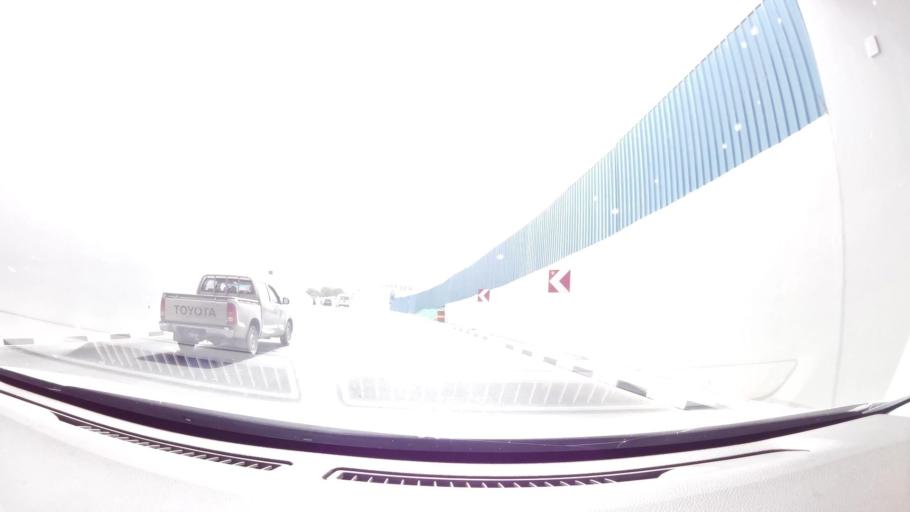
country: QA
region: Baladiyat ad Dawhah
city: Doha
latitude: 25.2960
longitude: 51.5150
